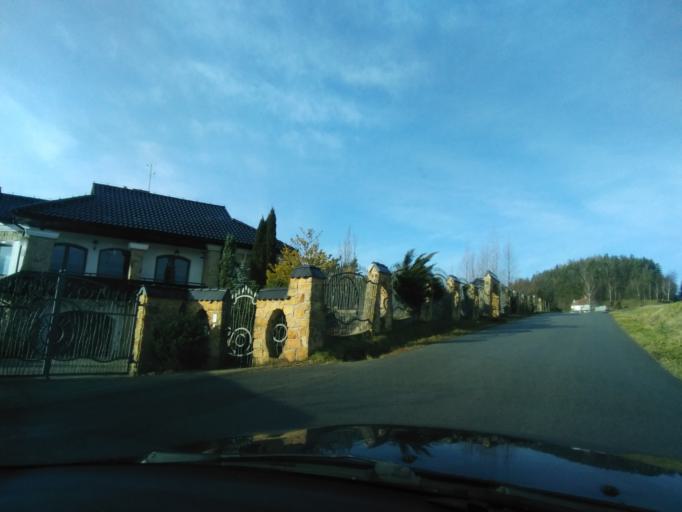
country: PL
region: Subcarpathian Voivodeship
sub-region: Powiat krosnienski
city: Korczyna
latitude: 49.7268
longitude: 21.7945
